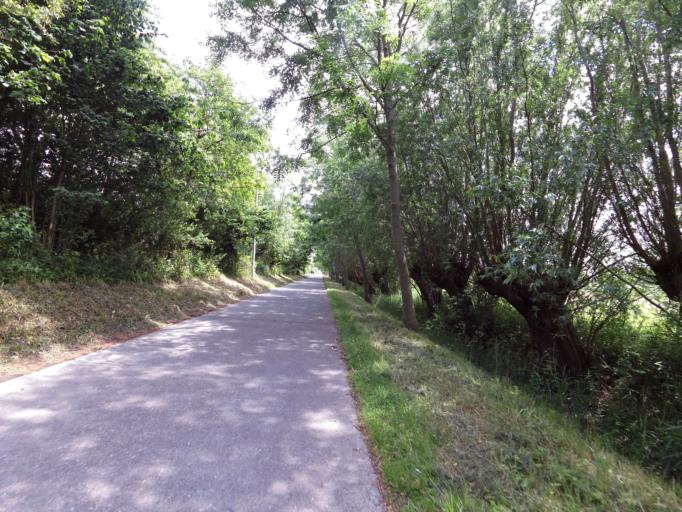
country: BE
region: Flanders
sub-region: Provincie West-Vlaanderen
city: Oudenburg
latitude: 51.1908
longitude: 2.9871
